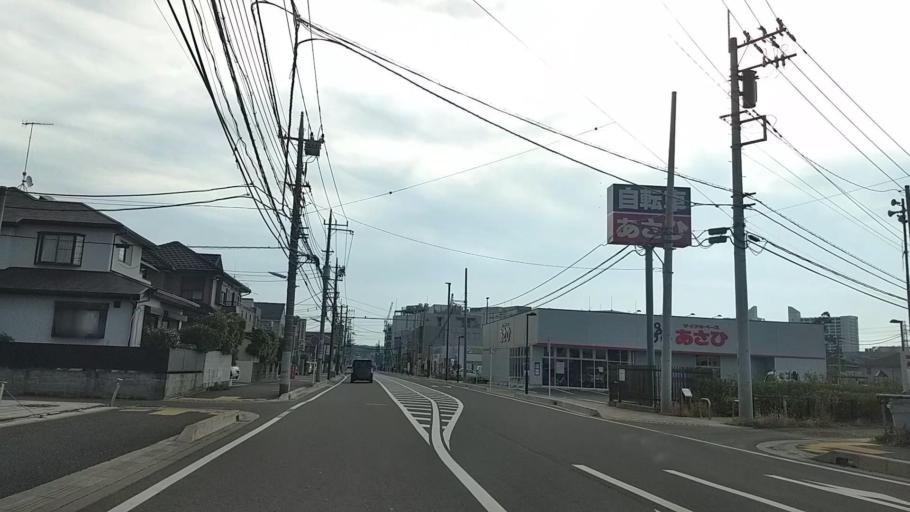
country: JP
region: Kanagawa
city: Zama
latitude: 35.4587
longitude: 139.3867
